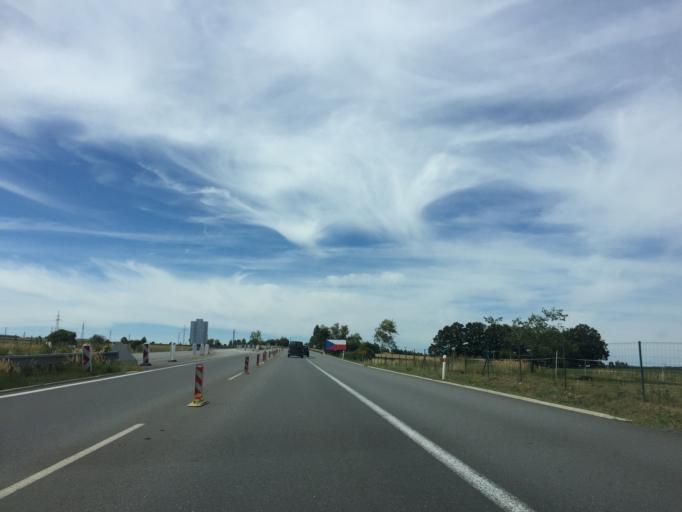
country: CZ
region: Jihocesky
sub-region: Okres Tabor
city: Sezimovo Usti
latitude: 49.4115
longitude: 14.7128
